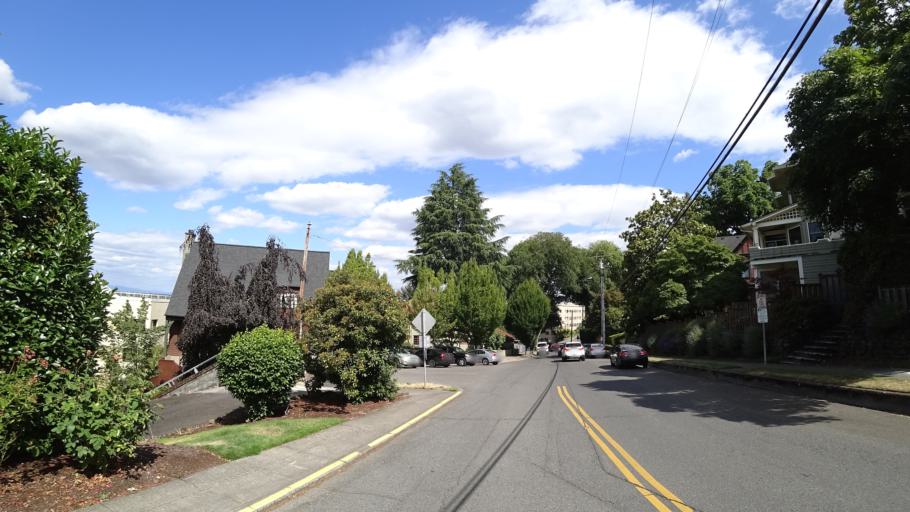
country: US
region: Oregon
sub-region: Multnomah County
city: Portland
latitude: 45.5289
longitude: -122.7039
